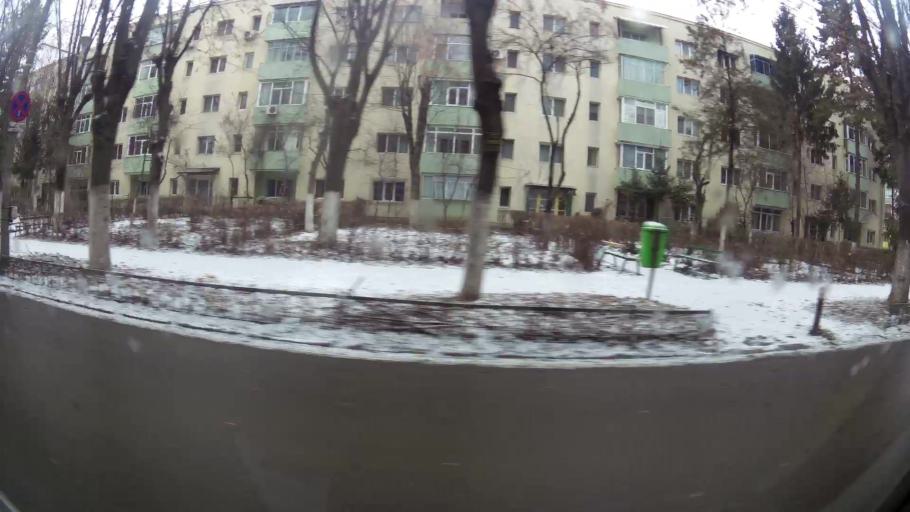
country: RO
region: Prahova
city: Ploiesti
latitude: 44.9587
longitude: 25.9994
